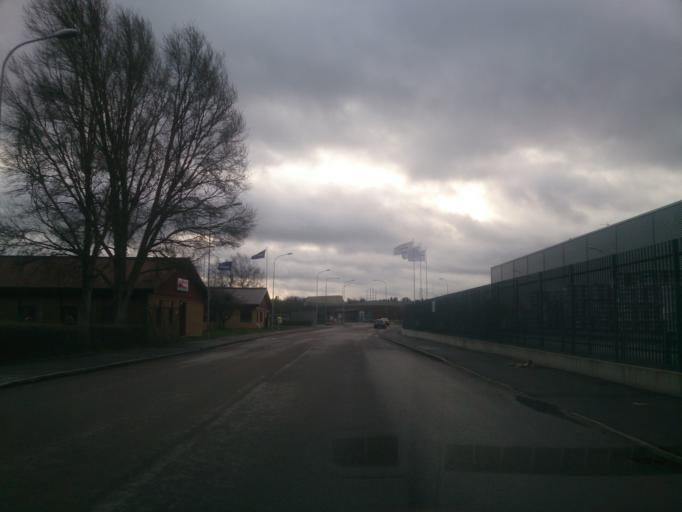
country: SE
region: OEstergoetland
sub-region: Norrkopings Kommun
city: Norrkoping
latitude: 58.5871
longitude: 16.2191
